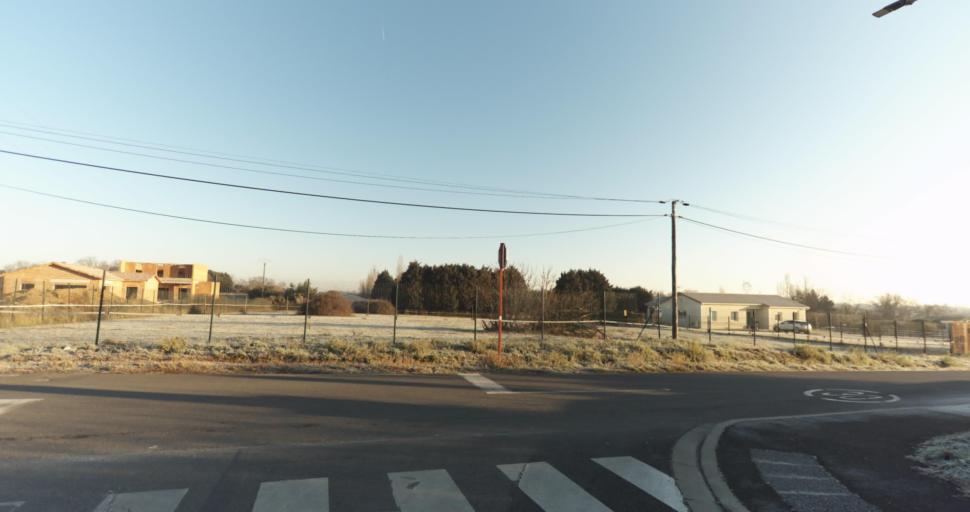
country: FR
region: Aquitaine
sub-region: Departement de la Gironde
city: Ambares-et-Lagrave
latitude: 44.9156
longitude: -0.4980
